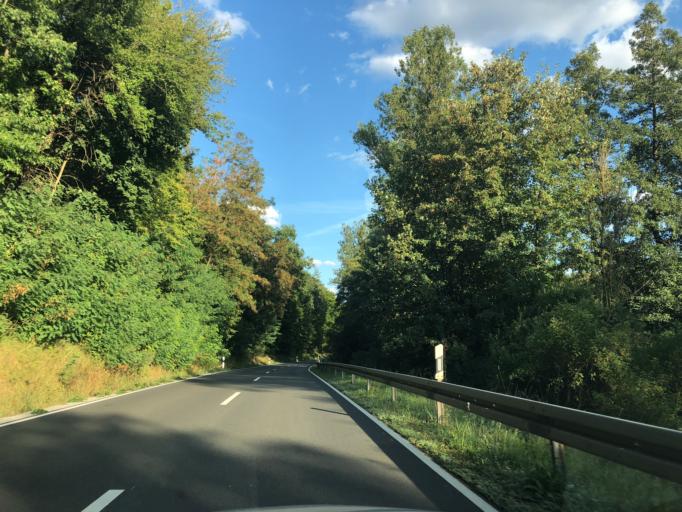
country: DE
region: Bavaria
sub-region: Upper Franconia
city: Burgwindheim
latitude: 49.8347
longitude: 10.5455
